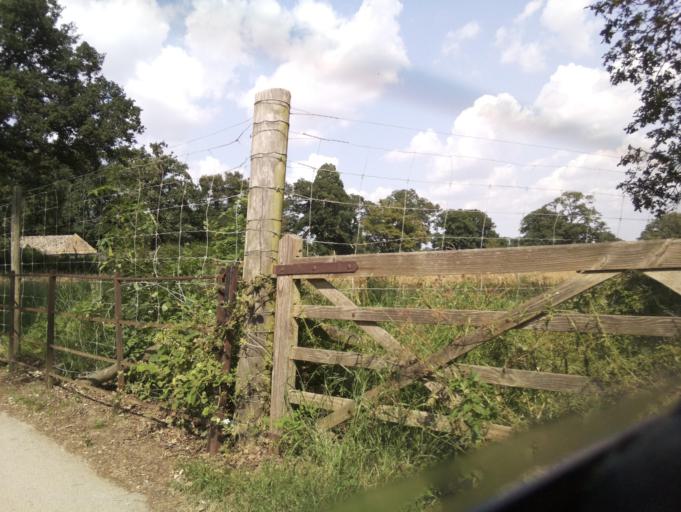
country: GB
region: England
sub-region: Gloucestershire
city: Moreton in Marsh
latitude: 51.9975
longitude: -1.7344
